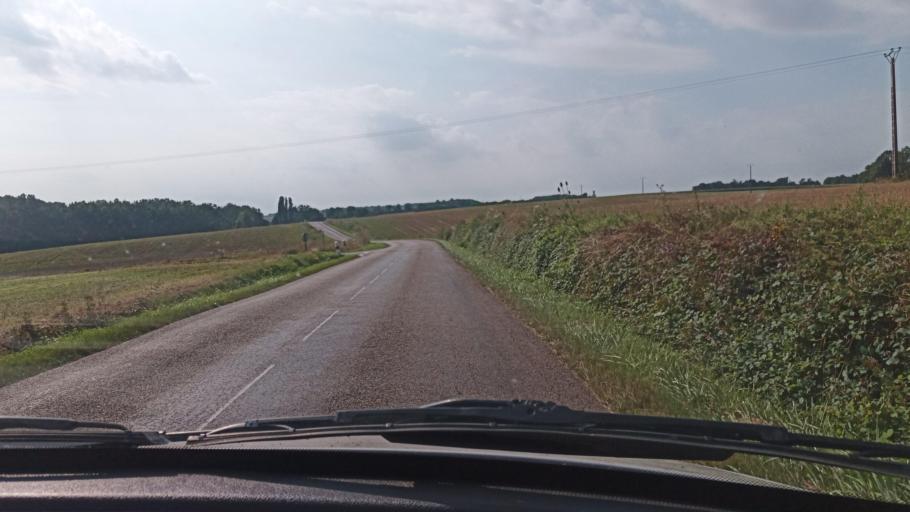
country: FR
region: Bourgogne
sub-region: Departement de l'Yonne
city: Saint-Valerien
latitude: 48.2061
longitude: 3.0763
